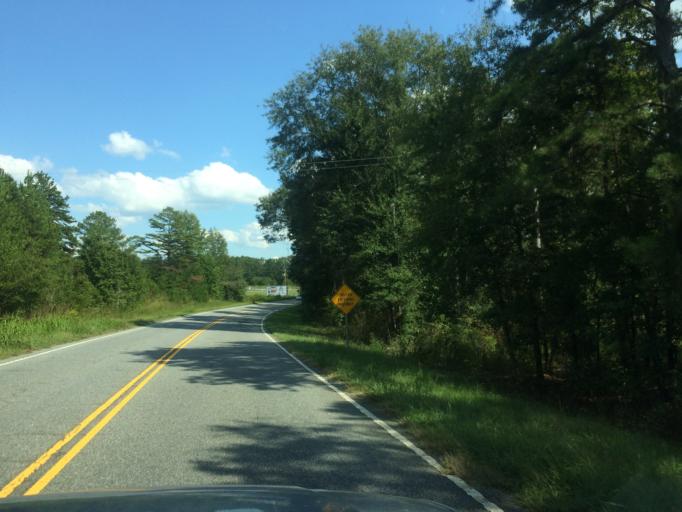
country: US
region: South Carolina
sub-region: Anderson County
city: Honea Path
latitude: 34.4730
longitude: -82.4325
